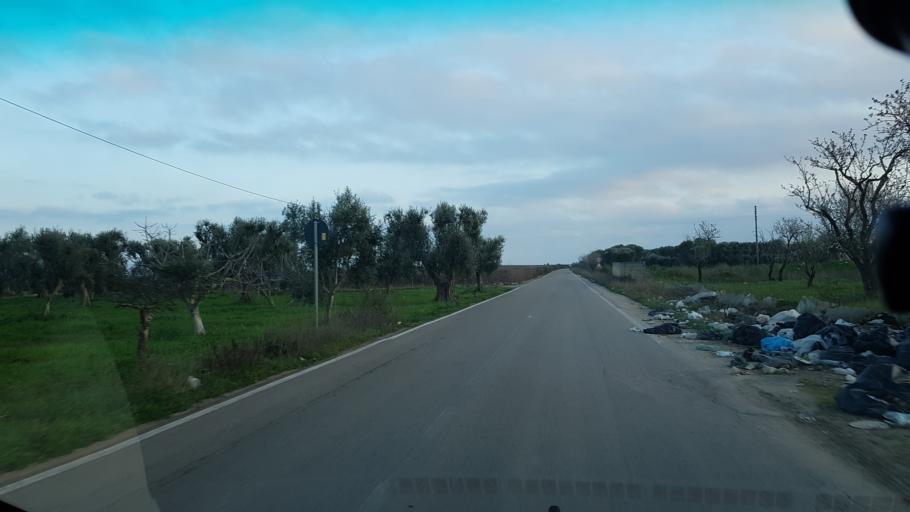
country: IT
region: Apulia
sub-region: Provincia di Brindisi
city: San Vito dei Normanni
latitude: 40.6374
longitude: 17.7806
